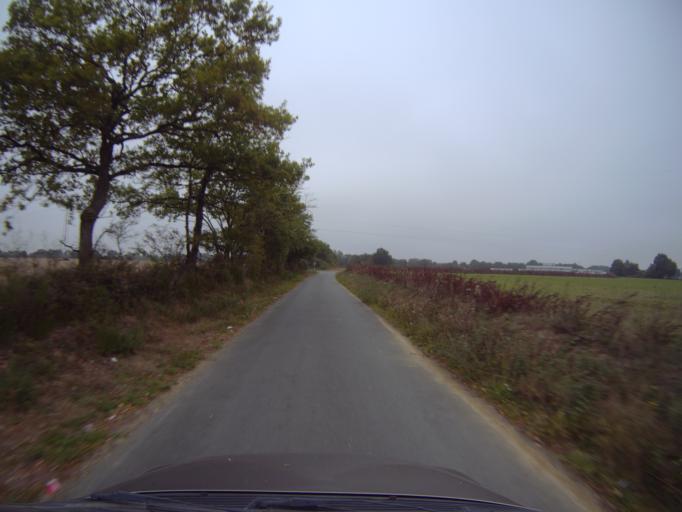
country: FR
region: Pays de la Loire
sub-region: Departement de la Vendee
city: Bouffere
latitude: 46.9746
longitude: -1.3418
